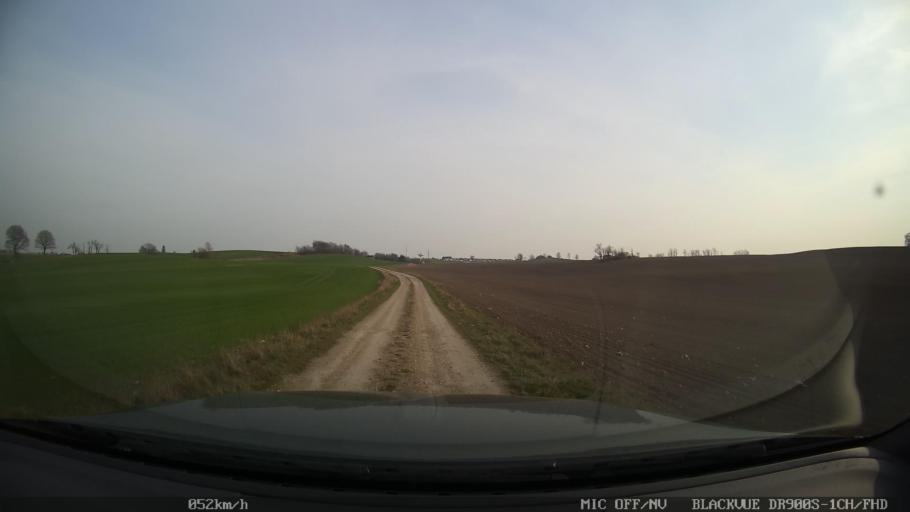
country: SE
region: Skane
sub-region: Ystads Kommun
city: Ystad
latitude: 55.4571
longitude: 13.7910
